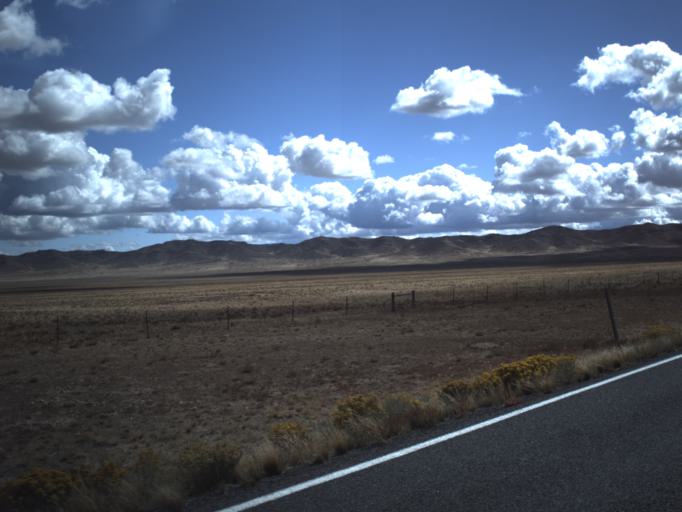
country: US
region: Utah
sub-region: Beaver County
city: Milford
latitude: 38.6757
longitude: -113.8885
